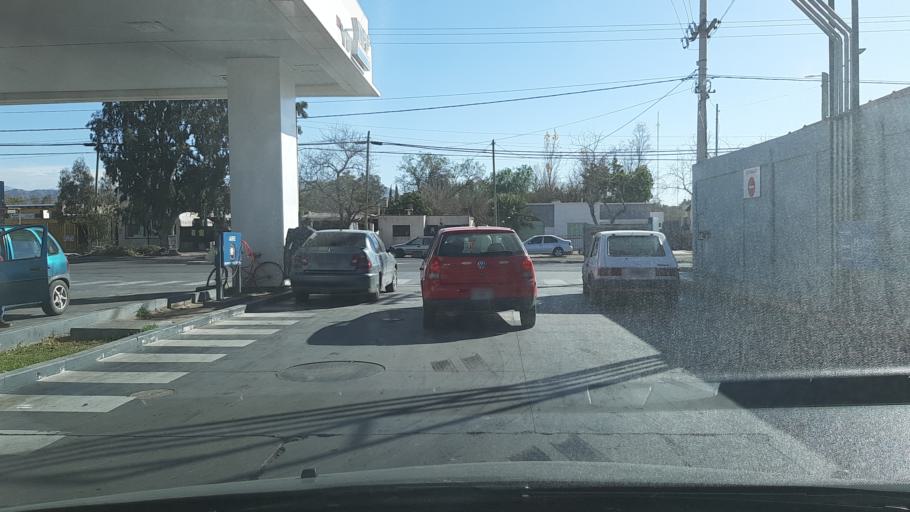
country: AR
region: San Juan
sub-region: Departamento de Rivadavia
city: Rivadavia
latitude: -31.5257
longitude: -68.6284
